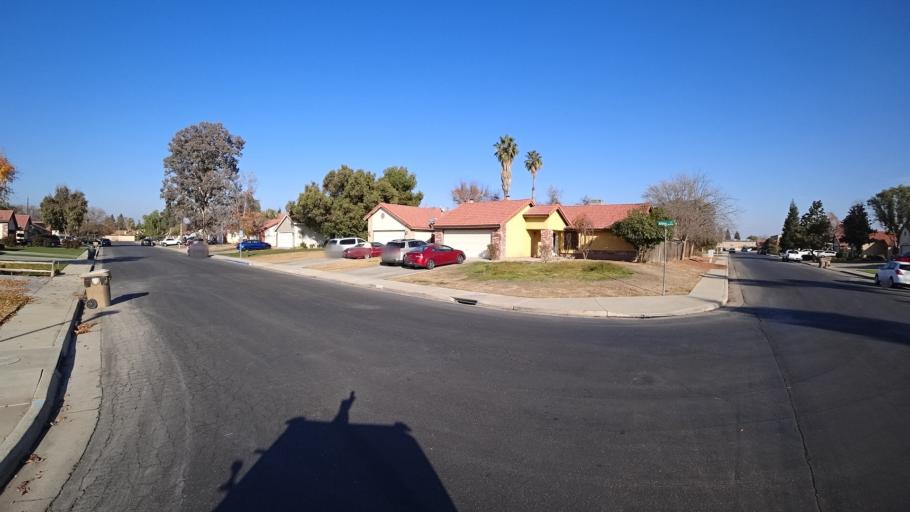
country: US
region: California
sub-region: Kern County
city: Greenacres
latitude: 35.3116
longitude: -119.0959
